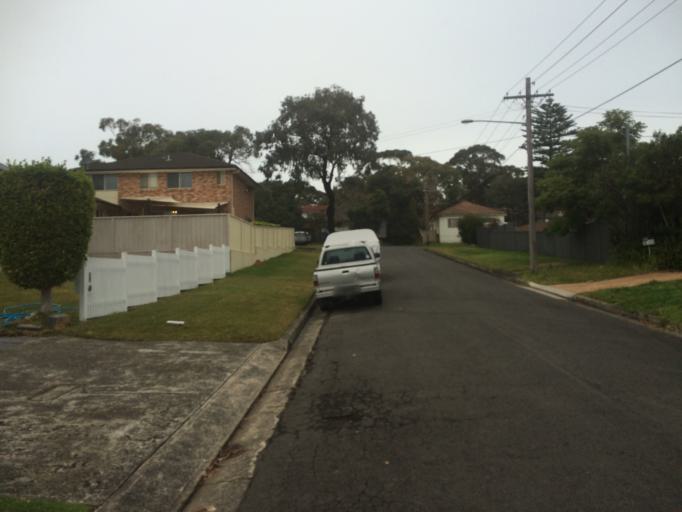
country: AU
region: New South Wales
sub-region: Sutherland Shire
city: Kirrawee
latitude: -34.0301
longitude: 151.0683
